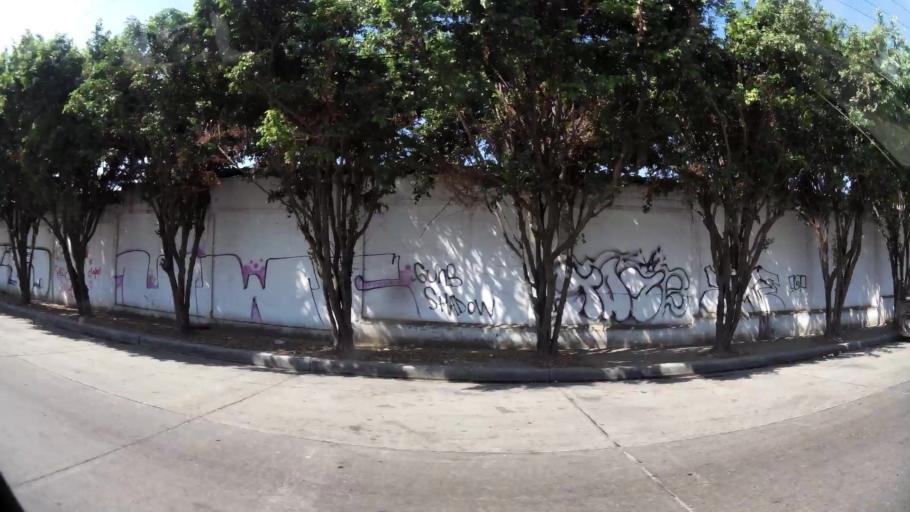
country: EC
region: Guayas
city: Guayaquil
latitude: -2.1222
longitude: -79.9297
